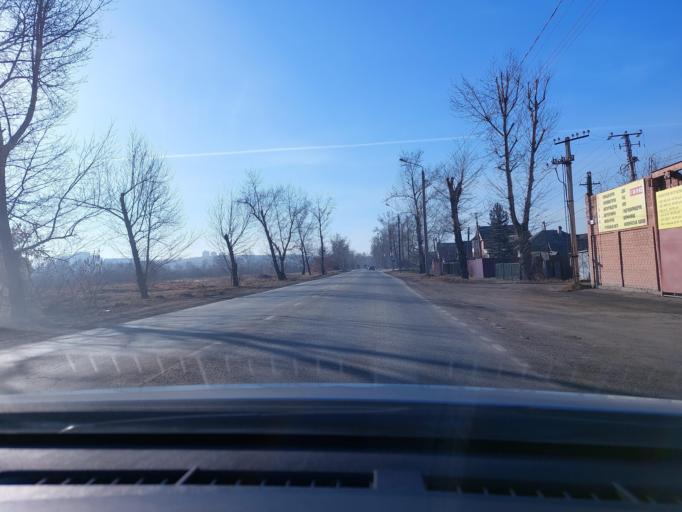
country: RU
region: Irkutsk
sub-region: Irkutskiy Rayon
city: Irkutsk
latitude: 52.3054
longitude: 104.2539
